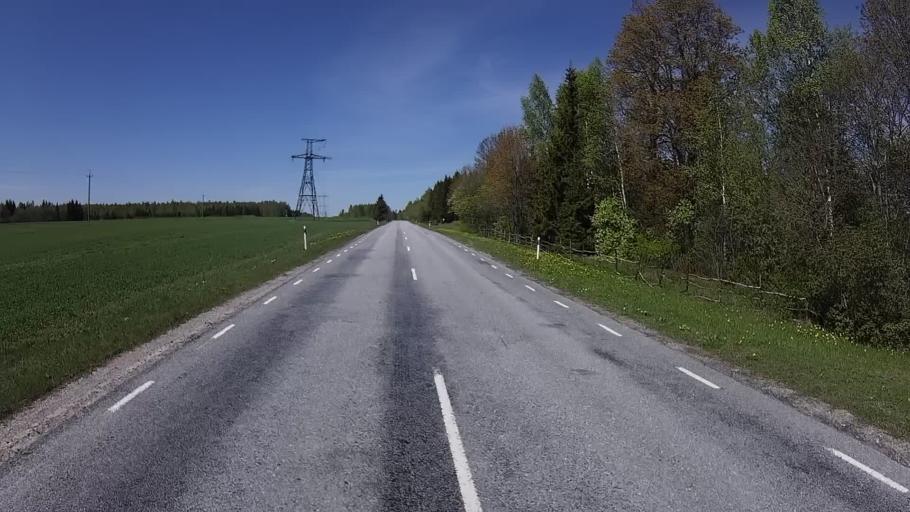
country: EE
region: Raplamaa
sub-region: Kehtna vald
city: Kehtna
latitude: 59.0398
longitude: 25.0381
